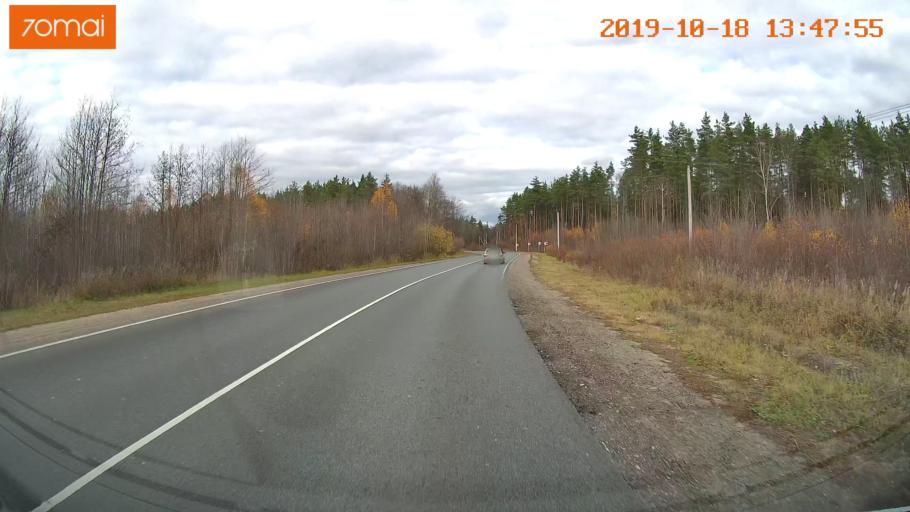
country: RU
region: Moskovskaya
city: Radovitskiy
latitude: 54.9823
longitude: 39.9516
